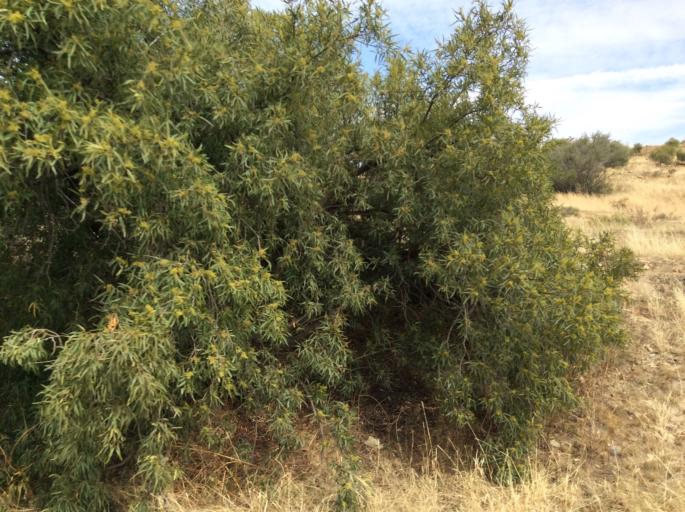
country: ZA
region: Orange Free State
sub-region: Xhariep District Municipality
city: Dewetsdorp
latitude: -29.5890
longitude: 26.6621
